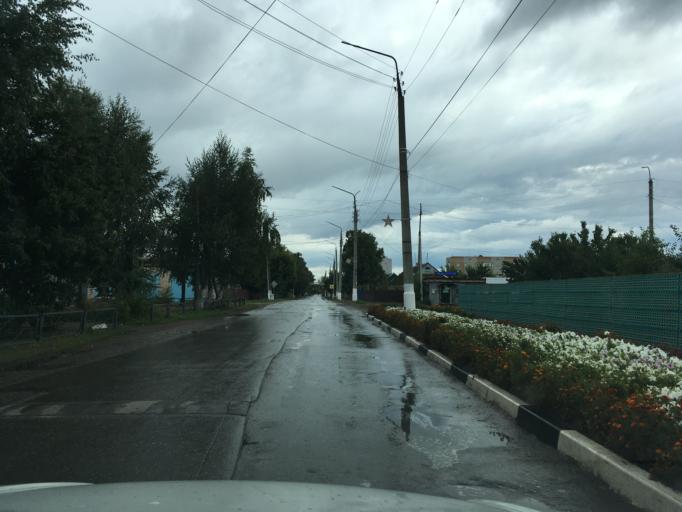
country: RU
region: Samara
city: Bezenchuk
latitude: 52.9832
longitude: 49.4395
